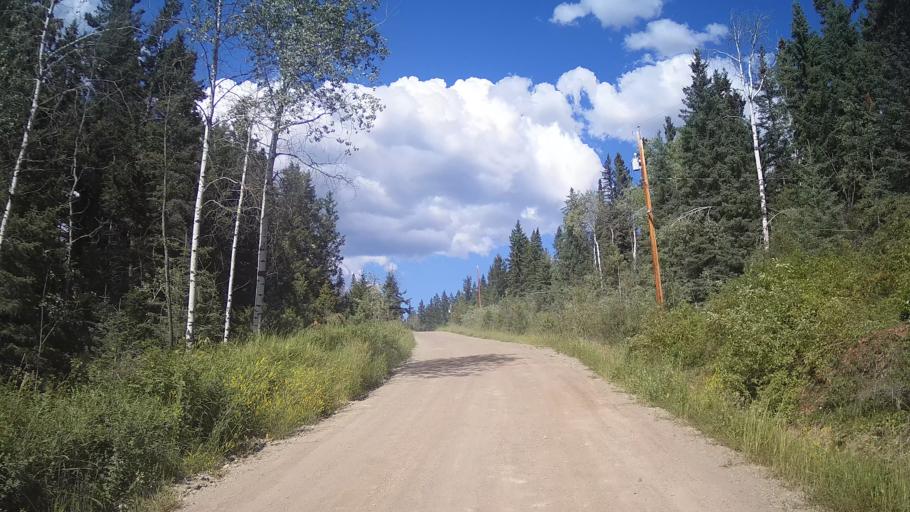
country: CA
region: British Columbia
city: Lillooet
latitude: 51.2639
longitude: -121.9826
